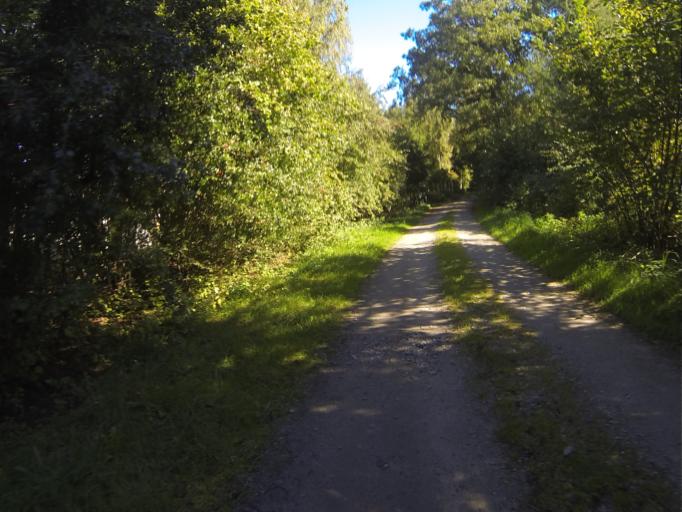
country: SE
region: Skane
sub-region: Hoors Kommun
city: Loberod
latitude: 55.7346
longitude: 13.3880
